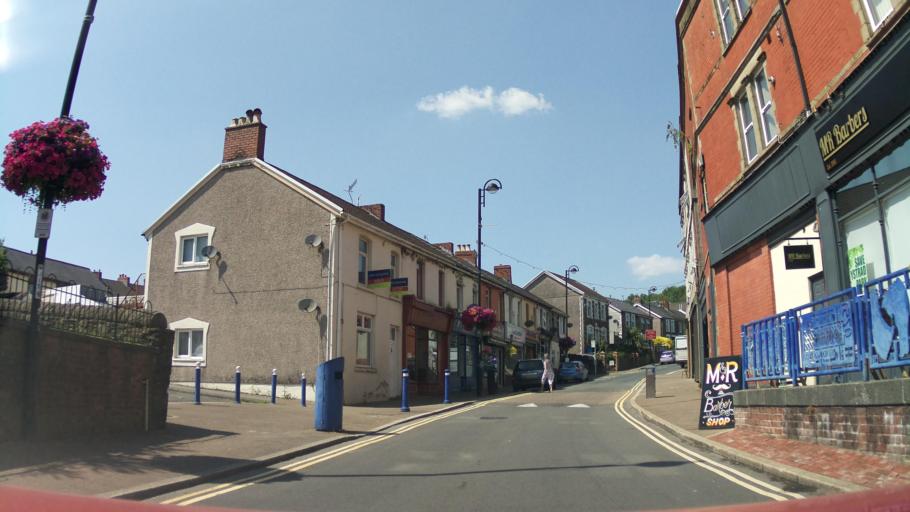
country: GB
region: Wales
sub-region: Caerphilly County Borough
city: Ystrad Mynach
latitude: 51.6414
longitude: -3.2365
